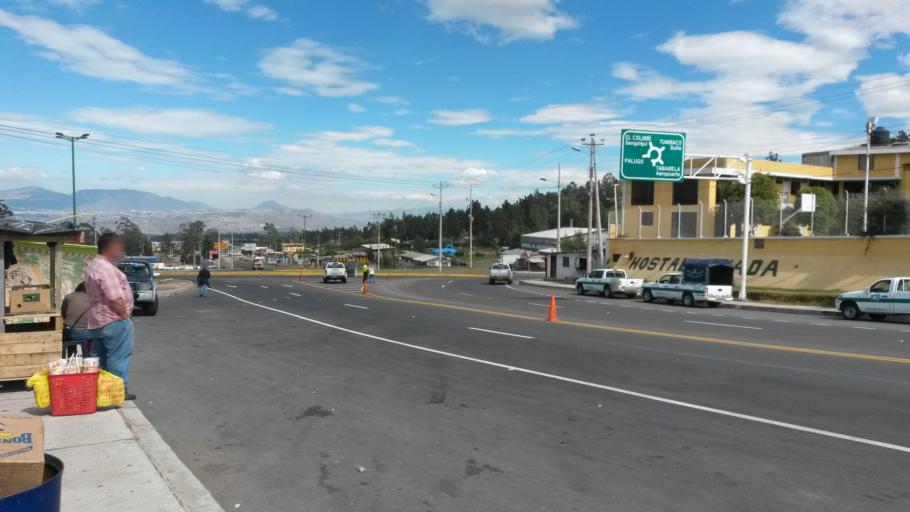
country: EC
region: Pichincha
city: Sangolqui
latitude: -0.2406
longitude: -78.3305
